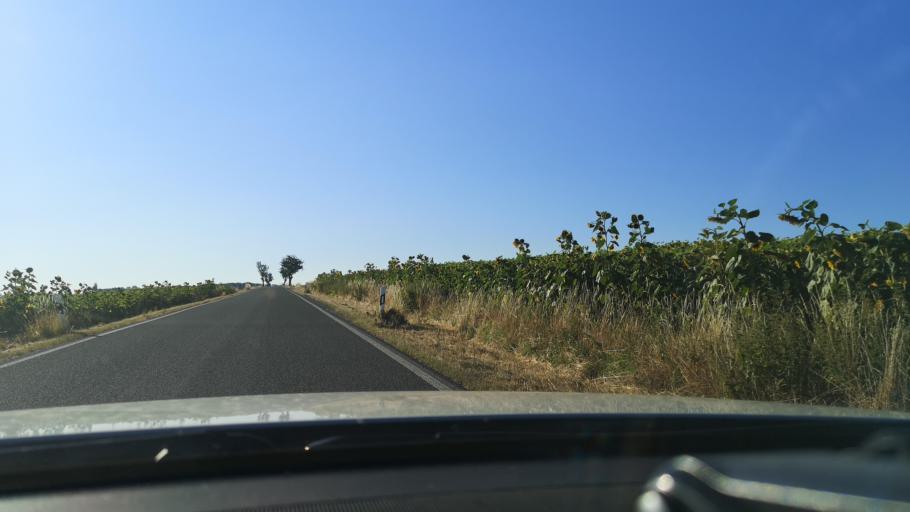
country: DE
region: Thuringia
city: Lehesten
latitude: 51.0244
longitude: 11.5703
